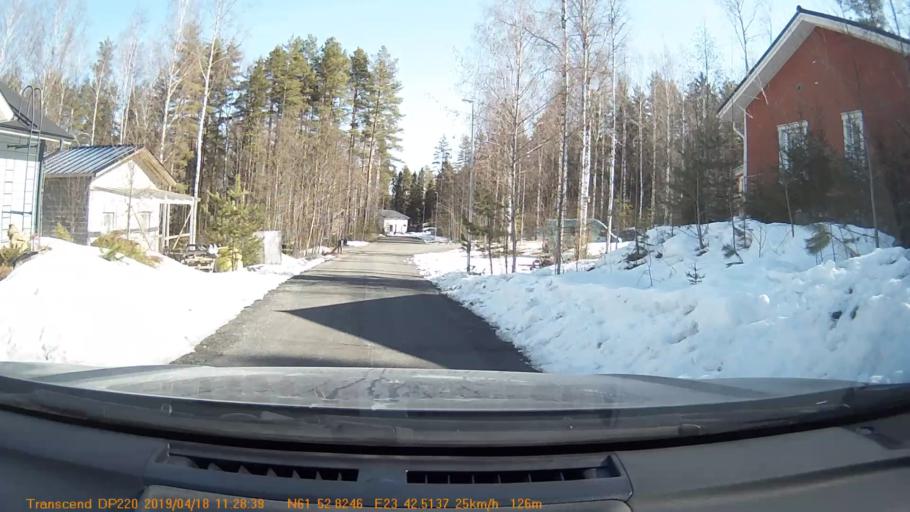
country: FI
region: Pirkanmaa
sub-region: Tampere
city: Kuru
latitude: 61.8804
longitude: 23.7085
